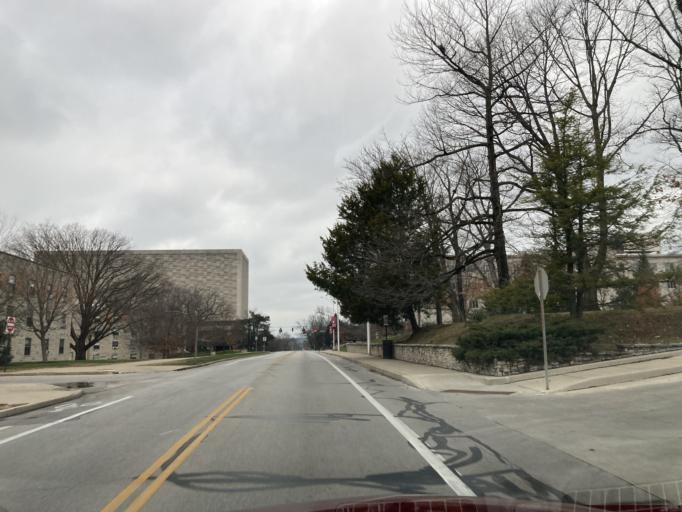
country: US
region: Indiana
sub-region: Monroe County
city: Bloomington
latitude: 39.1716
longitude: -86.5137
